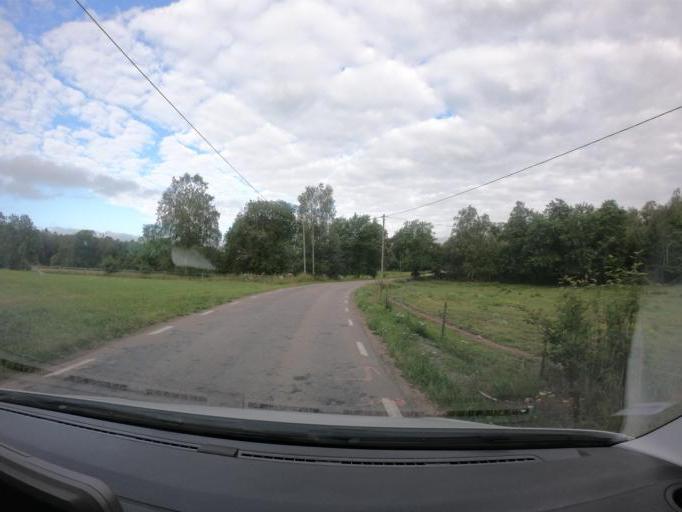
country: SE
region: Skane
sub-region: Angelholms Kommun
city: Munka-Ljungby
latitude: 56.3117
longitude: 13.0033
